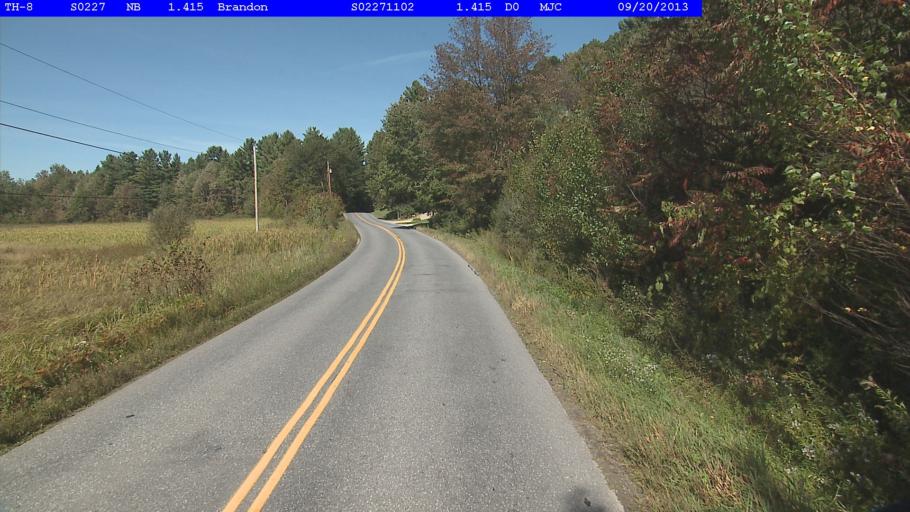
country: US
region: Vermont
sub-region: Rutland County
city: Brandon
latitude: 43.7949
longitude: -73.0540
